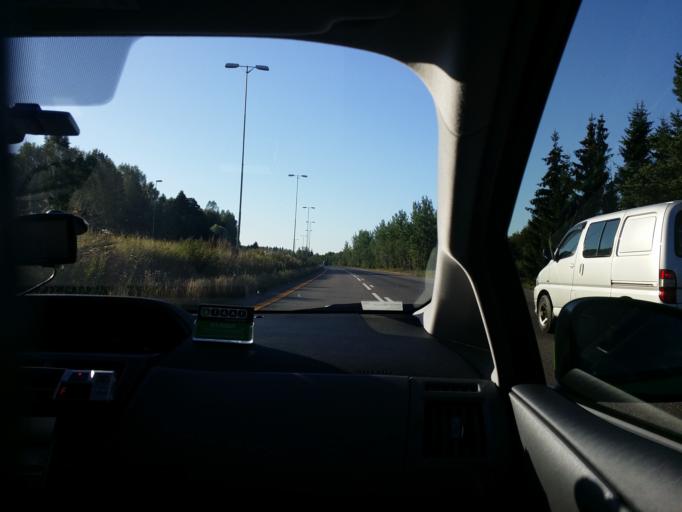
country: NO
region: Akershus
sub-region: Ullensaker
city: Jessheim
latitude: 60.1745
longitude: 11.0979
